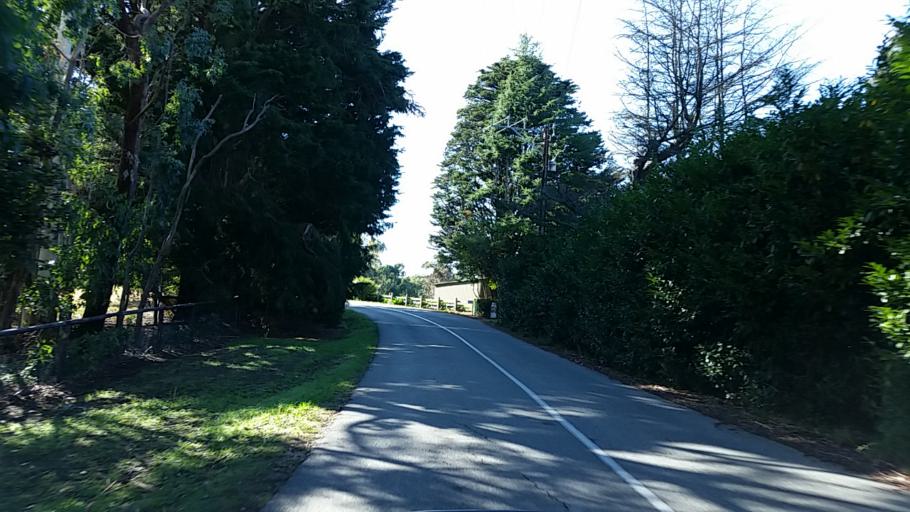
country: AU
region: South Australia
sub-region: Adelaide Hills
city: Adelaide Hills
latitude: -34.9446
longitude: 138.7263
